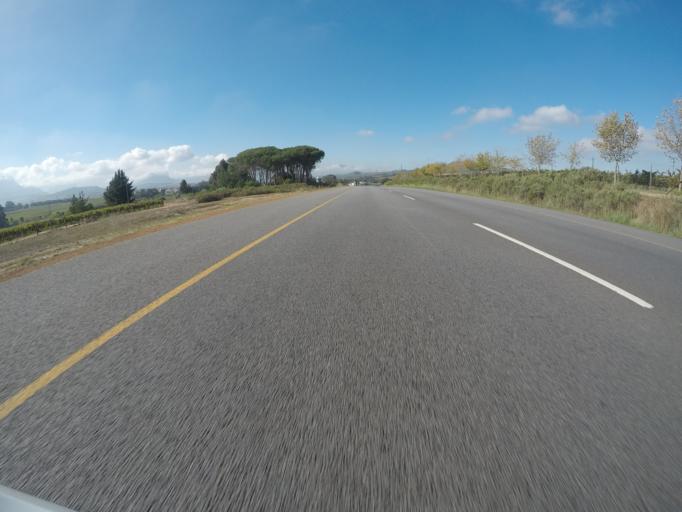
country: ZA
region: Western Cape
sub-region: Cape Winelands District Municipality
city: Stellenbosch
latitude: -33.8680
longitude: 18.8130
